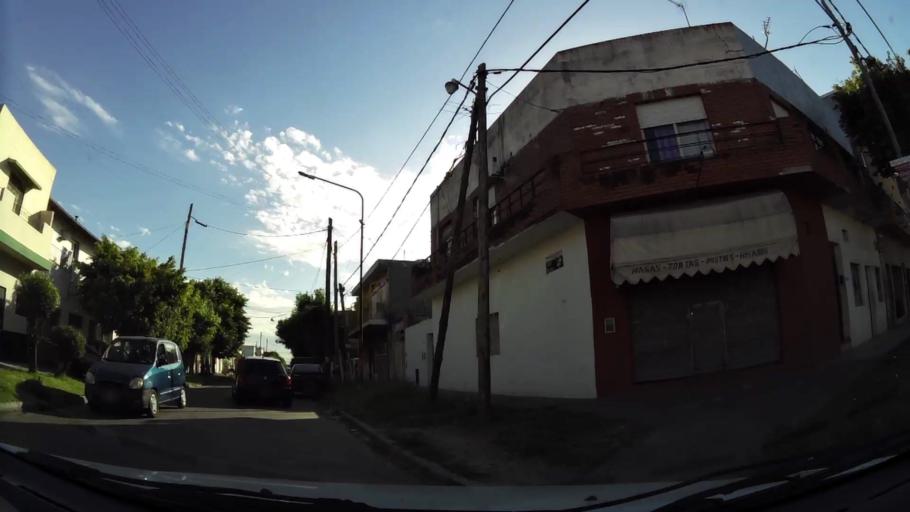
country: AR
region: Buenos Aires
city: Hurlingham
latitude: -34.5636
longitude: -58.6163
